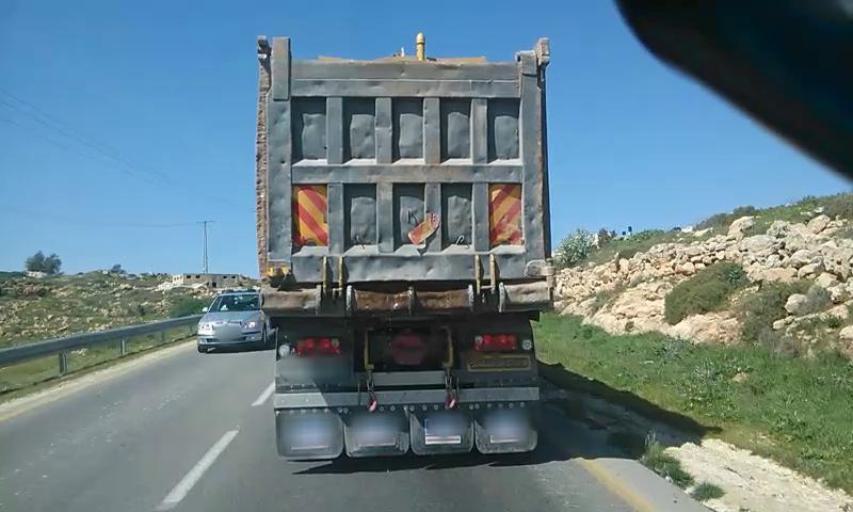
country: PS
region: West Bank
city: Jurat ash Sham`ah
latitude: 31.6478
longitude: 35.1757
